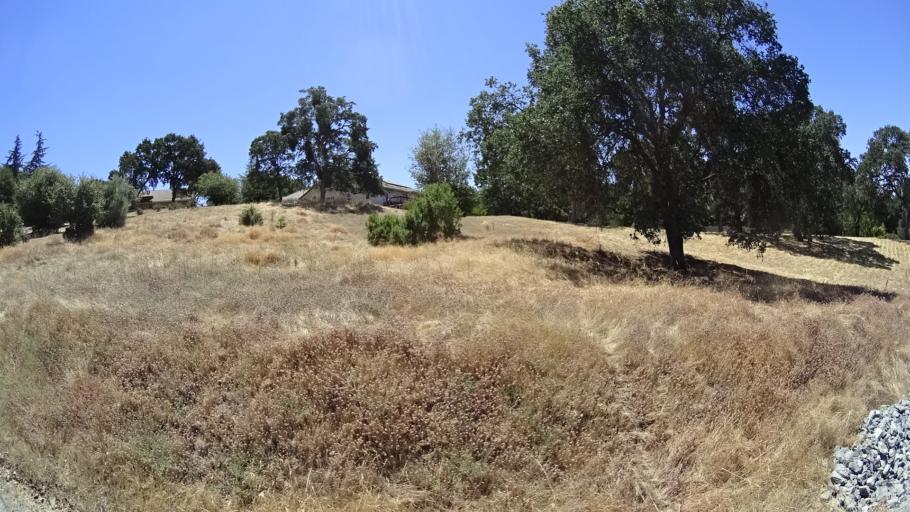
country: US
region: California
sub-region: Calaveras County
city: Valley Springs
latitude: 38.1661
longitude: -120.8240
